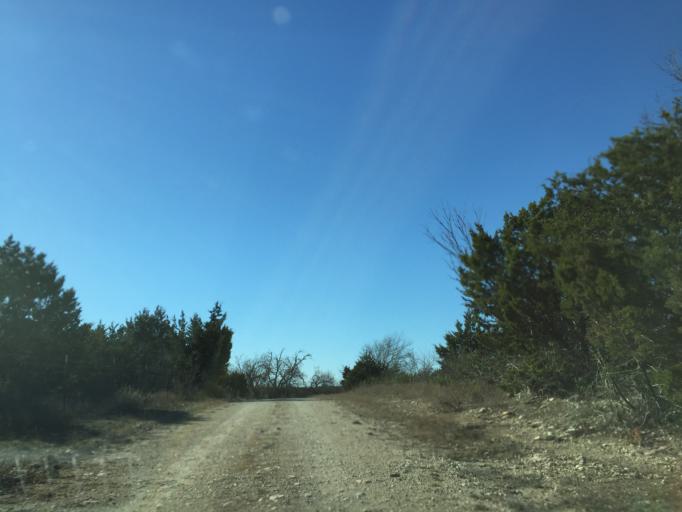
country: US
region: Texas
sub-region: Lampasas County
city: Lampasas
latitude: 30.9425
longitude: -98.1613
